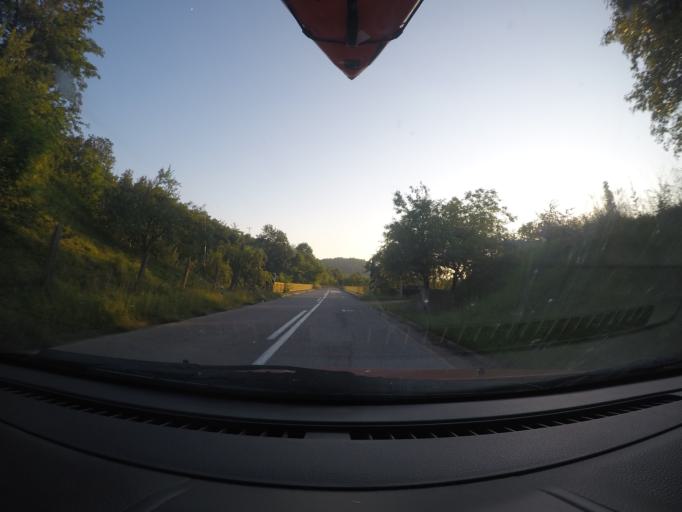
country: RO
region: Mehedinti
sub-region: Comuna Eselnita
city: Eselnita
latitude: 44.6677
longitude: 22.3629
